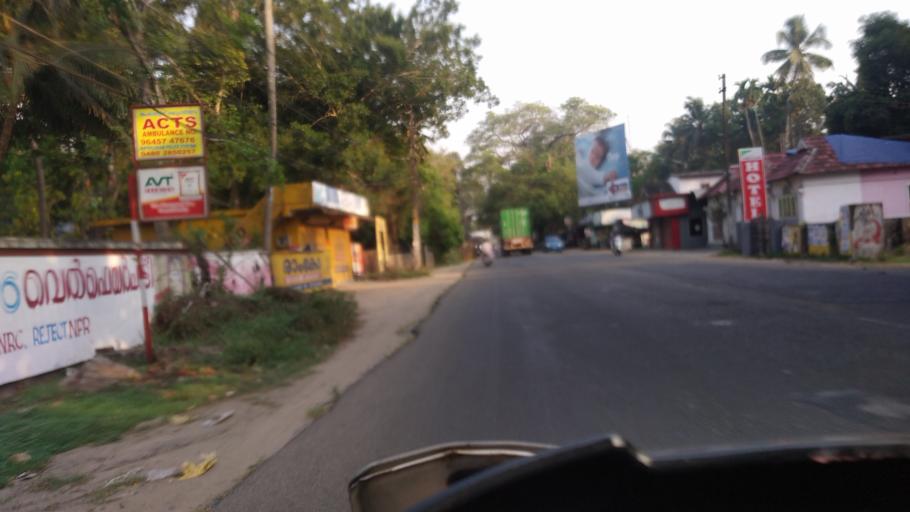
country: IN
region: Kerala
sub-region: Thrissur District
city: Irinjalakuda
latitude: 10.3334
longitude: 76.1401
